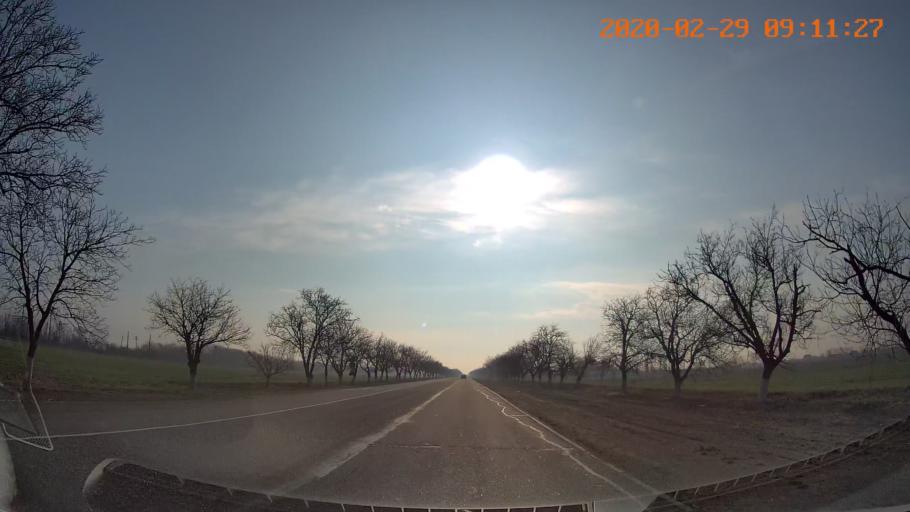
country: MD
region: Telenesti
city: Slobozia
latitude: 46.8350
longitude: 29.8001
